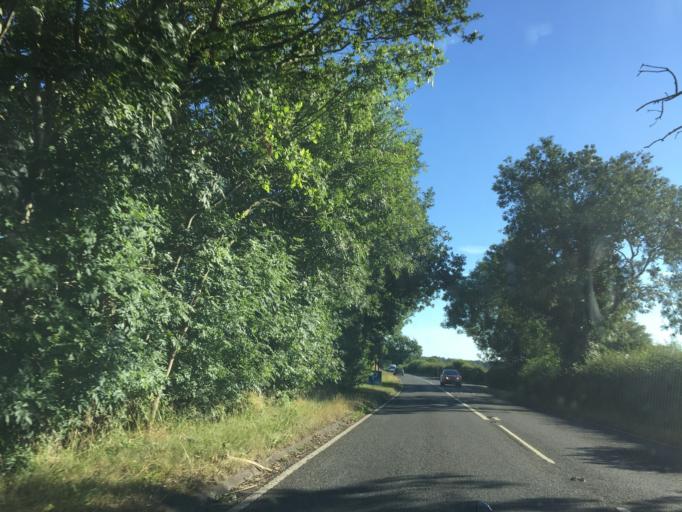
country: GB
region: England
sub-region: Warwickshire
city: Royal Leamington Spa
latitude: 52.3216
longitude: -1.5287
